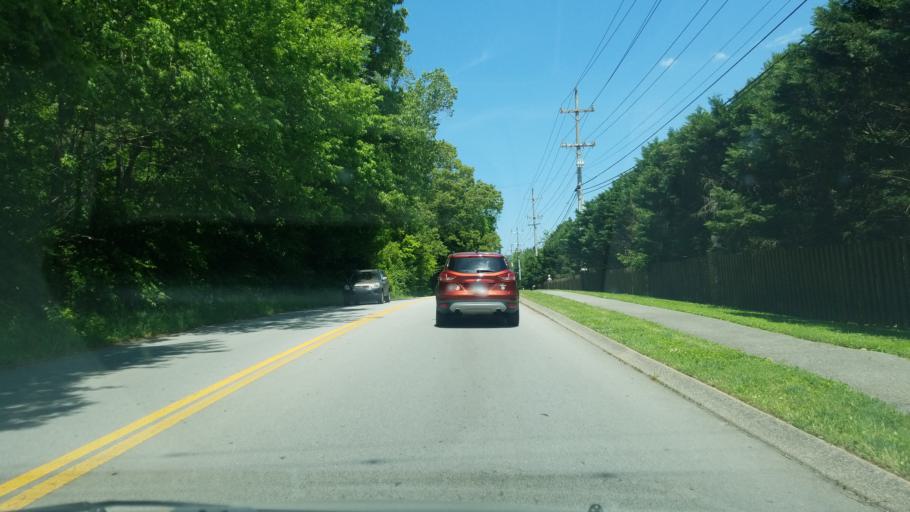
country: US
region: Tennessee
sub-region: Hamilton County
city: Signal Mountain
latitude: 35.1035
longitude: -85.3274
